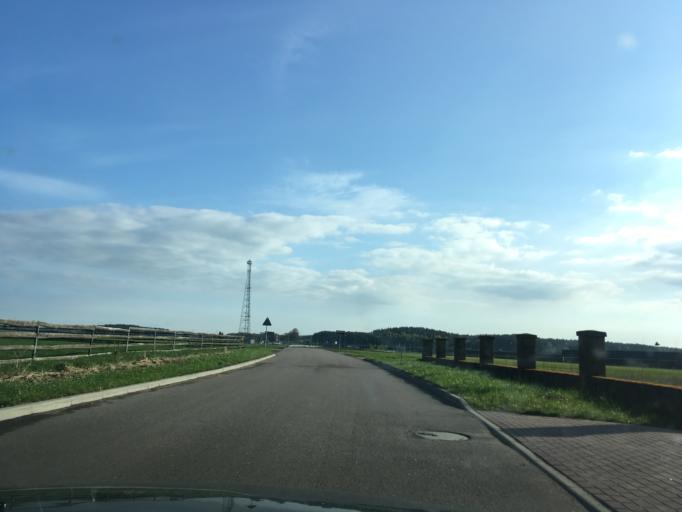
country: PL
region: Warmian-Masurian Voivodeship
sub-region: Powiat nidzicki
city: Nidzica
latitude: 53.4086
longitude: 20.3333
